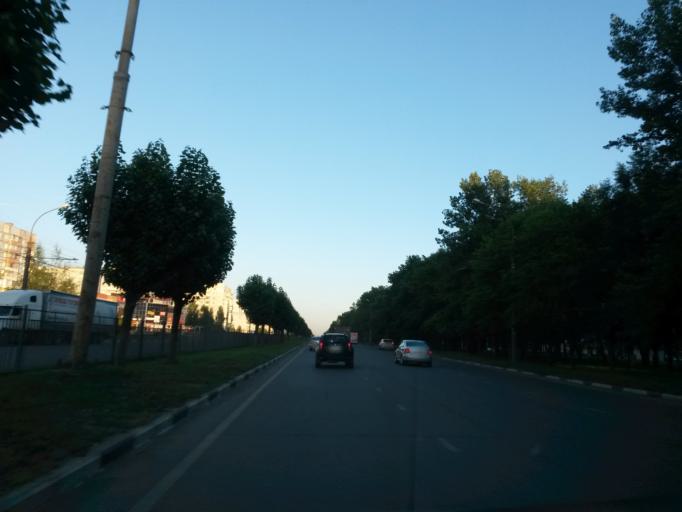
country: RU
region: Jaroslavl
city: Yaroslavl
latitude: 57.6948
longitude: 39.7692
